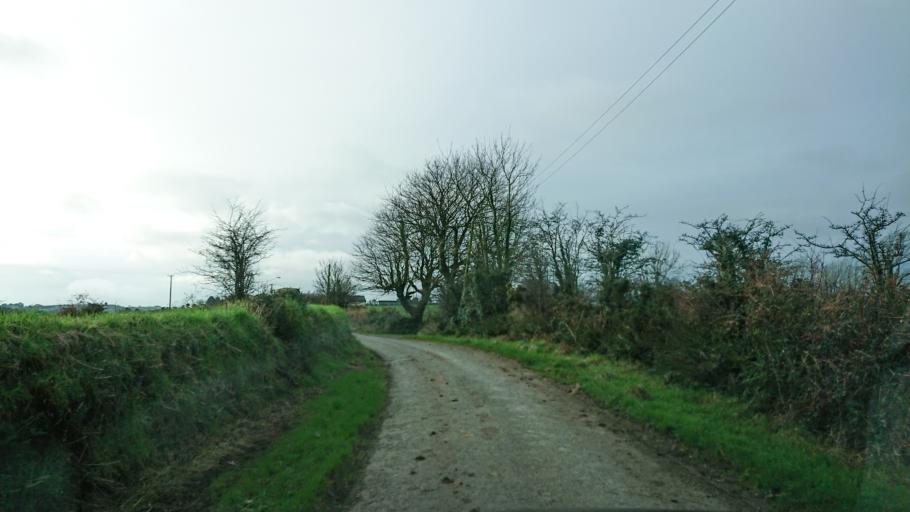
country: IE
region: Munster
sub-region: Waterford
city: Tra Mhor
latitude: 52.1944
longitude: -7.1725
